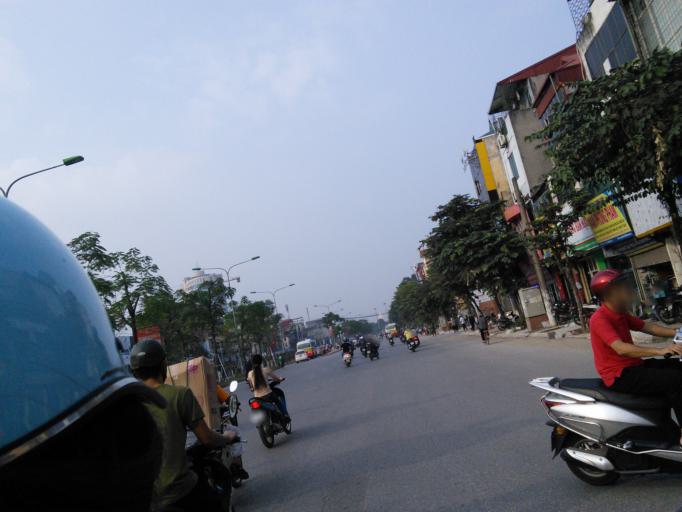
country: VN
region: Ha Noi
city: Hai BaTrung
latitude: 21.0031
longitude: 105.8415
